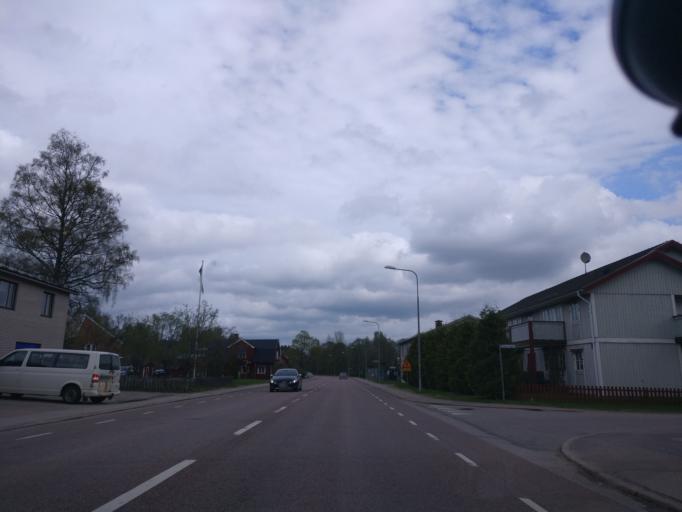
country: SE
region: Vaermland
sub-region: Hagfors Kommun
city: Ekshaerad
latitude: 60.1776
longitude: 13.4960
